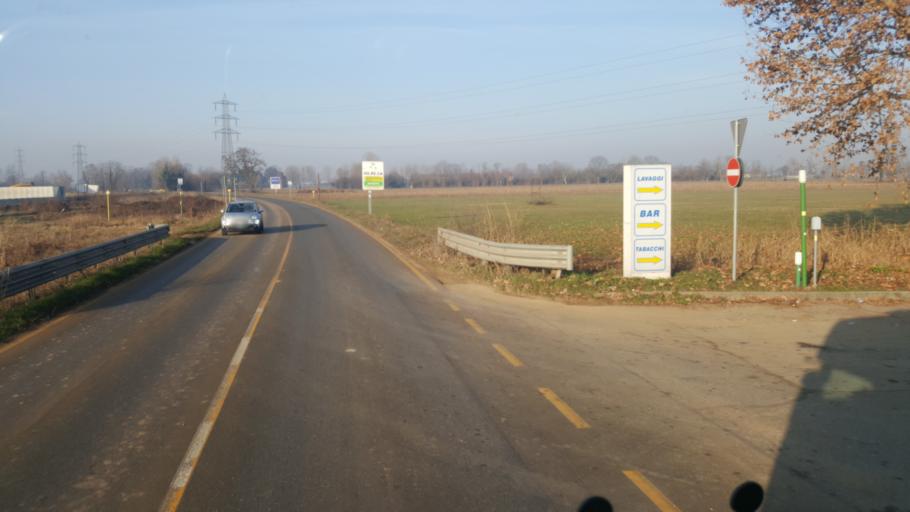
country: IT
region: Lombardy
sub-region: Citta metropolitana di Milano
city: Villaggio Residenziale
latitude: 45.5232
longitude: 9.4640
